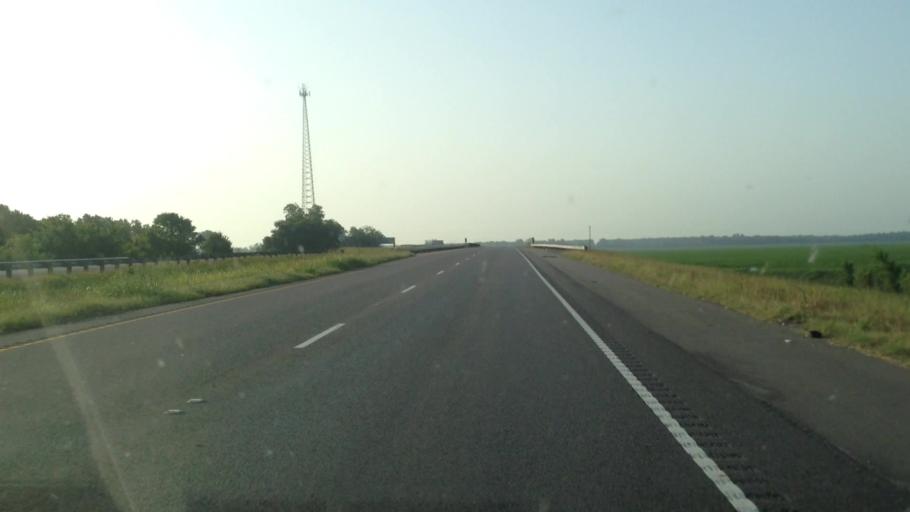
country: US
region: Louisiana
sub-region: Rapides Parish
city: Boyce
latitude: 31.3937
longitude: -92.6948
